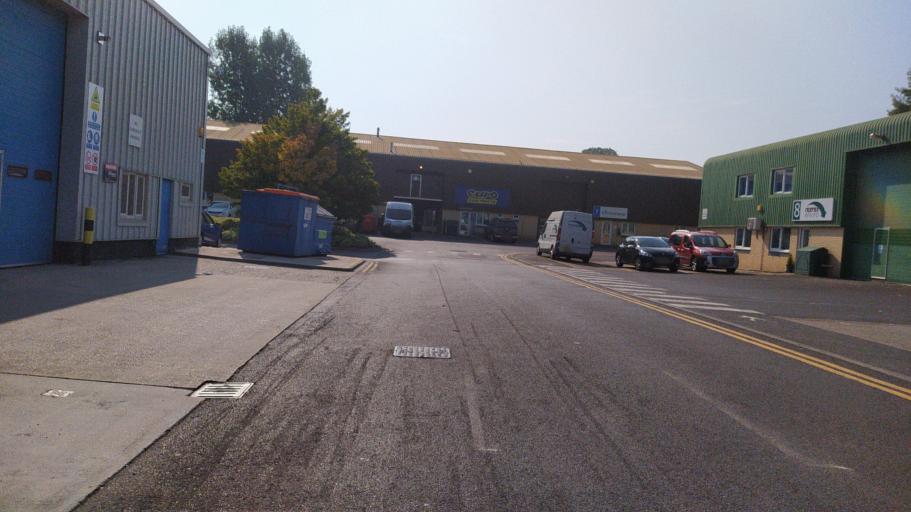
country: GB
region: England
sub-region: Hampshire
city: Andover
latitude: 51.2029
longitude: -1.4858
